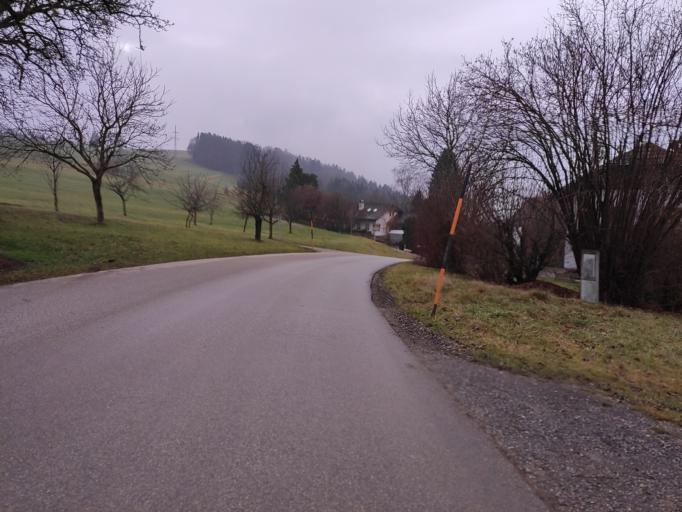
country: AT
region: Salzburg
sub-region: Politischer Bezirk Salzburg-Umgebung
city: Kostendorf
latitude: 47.9273
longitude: 13.2165
